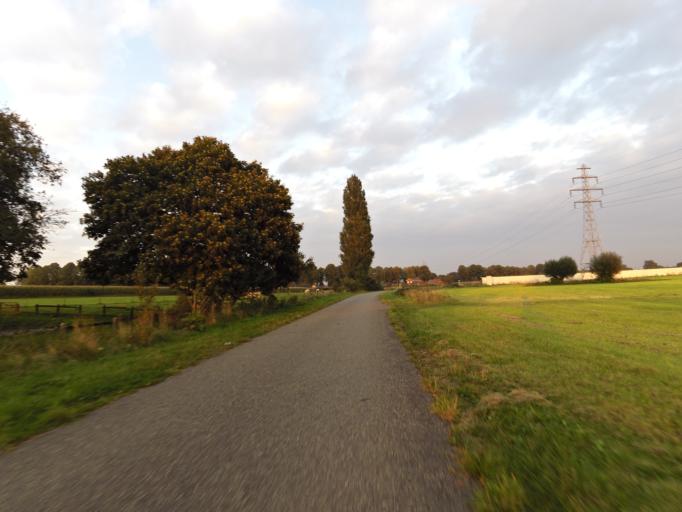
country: NL
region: Gelderland
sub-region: Gemeente Doetinchem
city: Doetinchem
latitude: 51.9519
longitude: 6.2271
